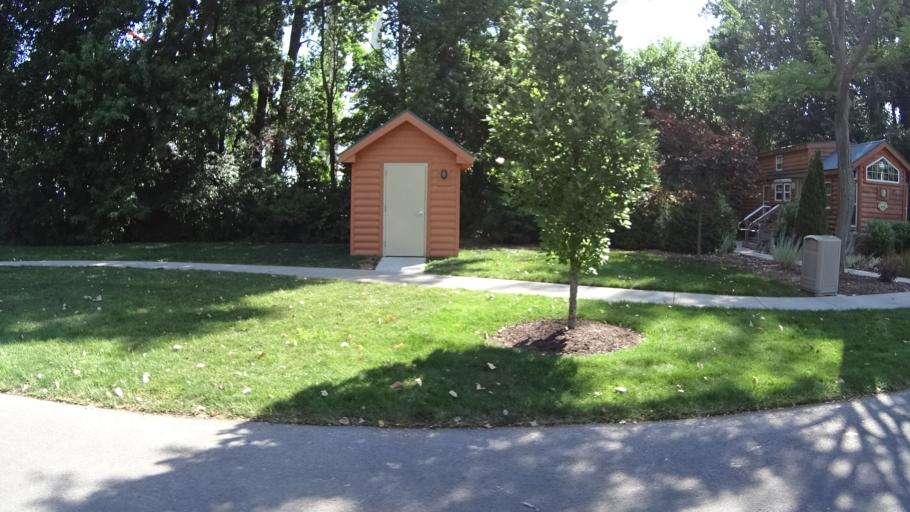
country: US
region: Ohio
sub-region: Erie County
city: Sandusky
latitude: 41.4898
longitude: -82.6870
